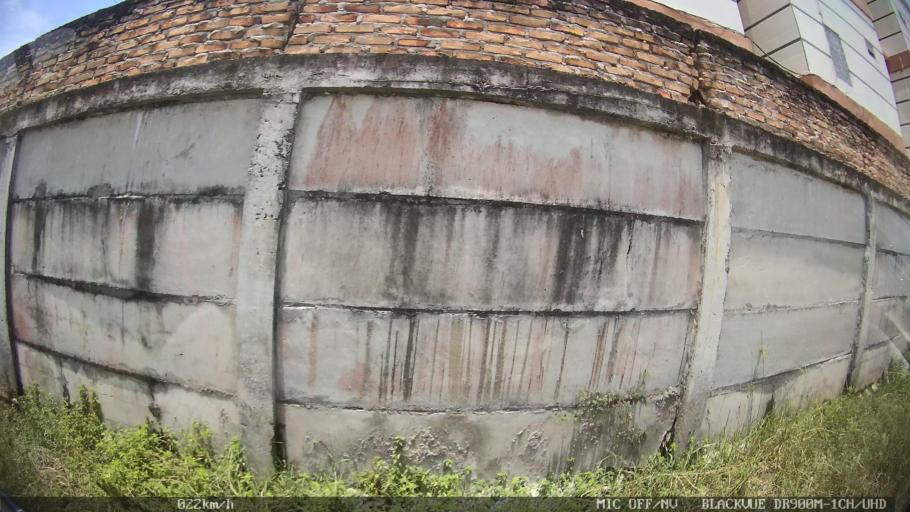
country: ID
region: North Sumatra
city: Percut
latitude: 3.5495
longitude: 98.8539
